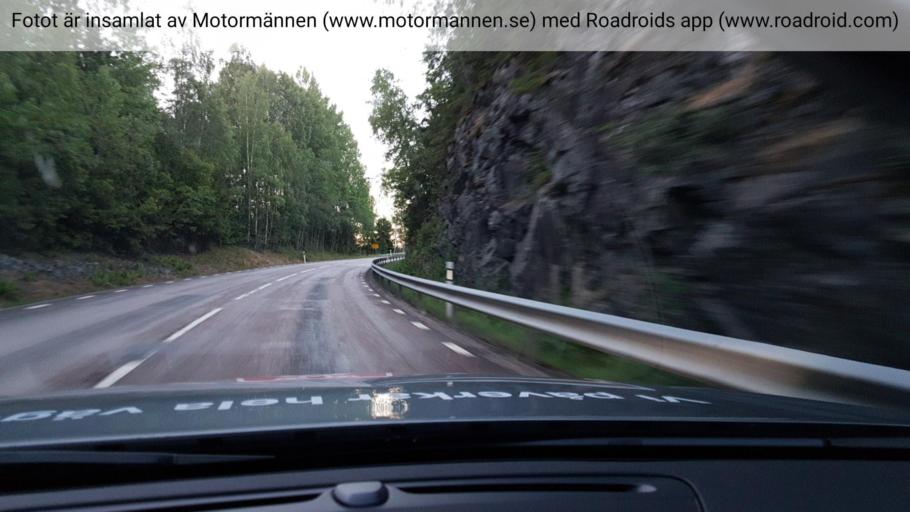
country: SE
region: Vaestmanland
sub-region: Skinnskattebergs Kommun
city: Skinnskatteberg
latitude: 59.8945
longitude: 15.6873
